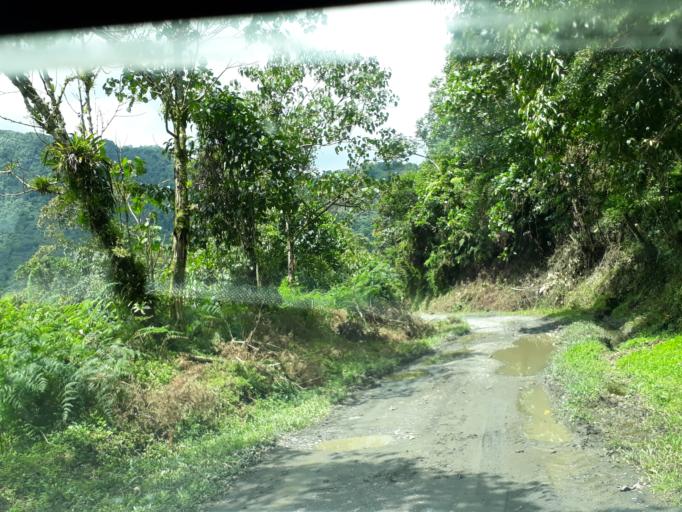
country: CO
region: Cundinamarca
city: Topaipi
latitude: 5.3165
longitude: -74.2132
